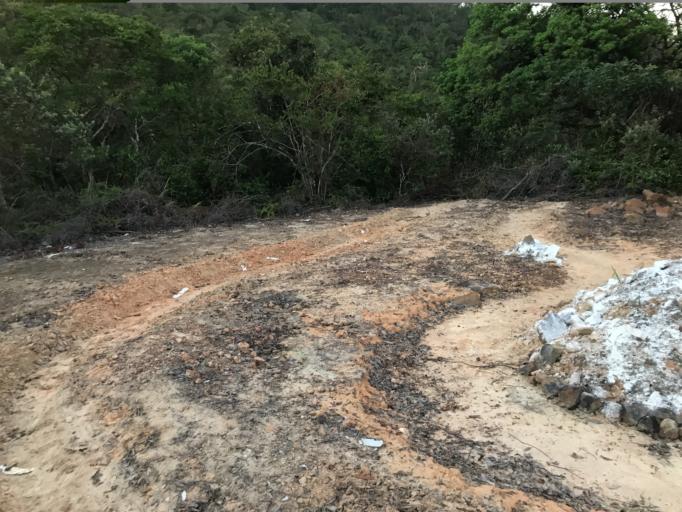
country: HK
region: Tai Po
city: Tai Po
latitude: 22.4721
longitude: 114.1457
